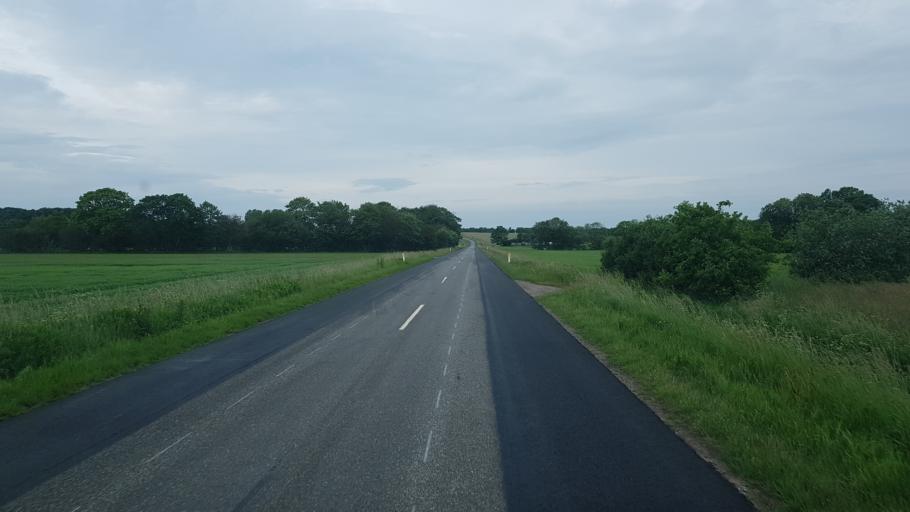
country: DK
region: South Denmark
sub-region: Vejen Kommune
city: Brorup
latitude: 55.4406
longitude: 8.9570
